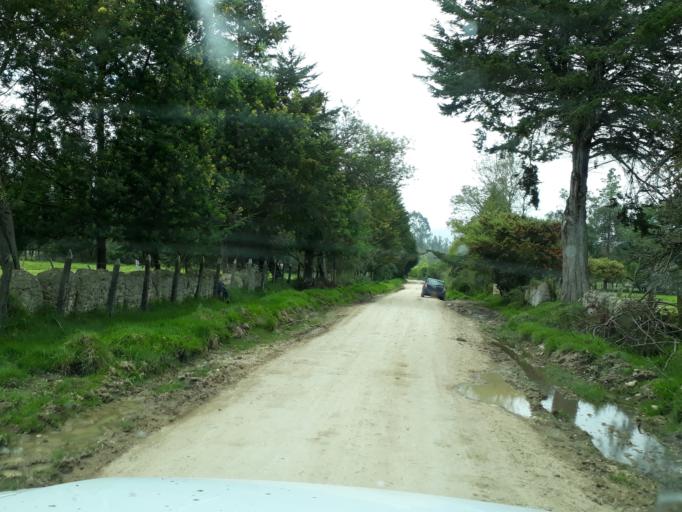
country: CO
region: Cundinamarca
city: Guasca
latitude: 4.8576
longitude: -73.8915
